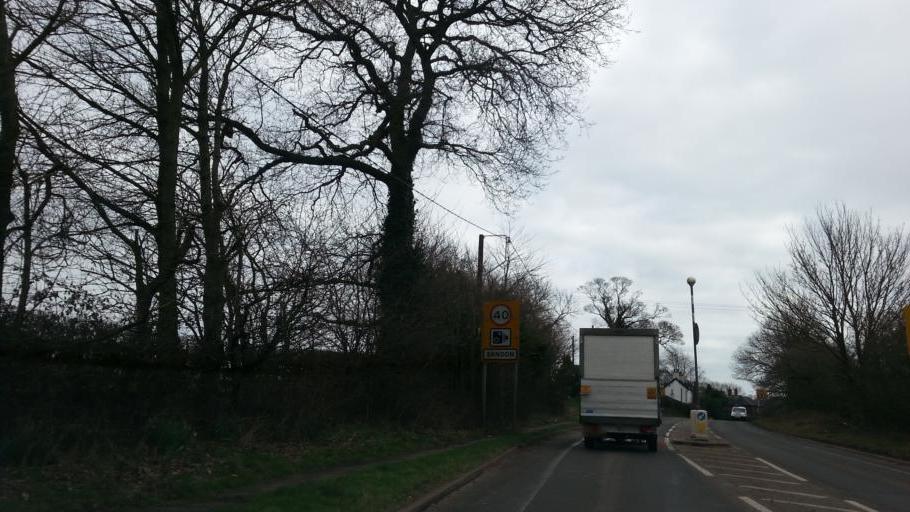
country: GB
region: England
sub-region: Staffordshire
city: Stafford
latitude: 52.8671
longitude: -2.0841
